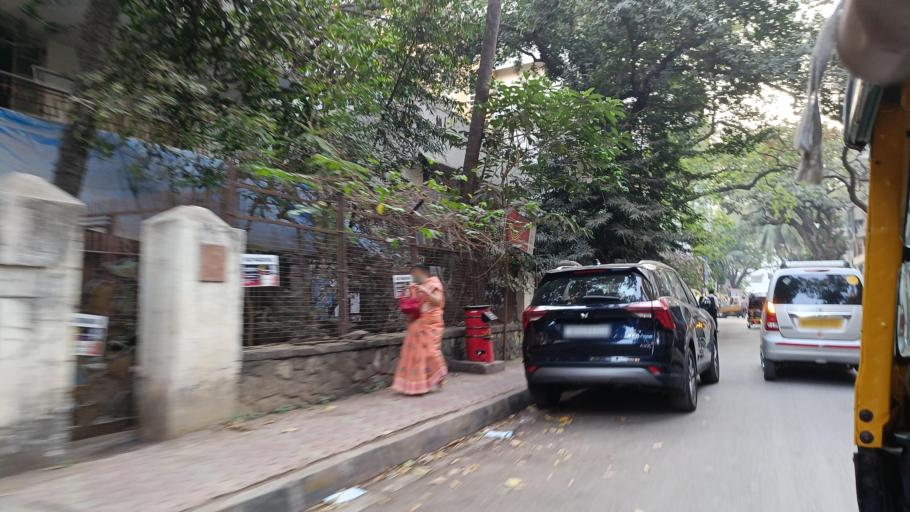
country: IN
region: Maharashtra
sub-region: Mumbai Suburban
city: Mumbai
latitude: 19.0701
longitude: 72.8353
